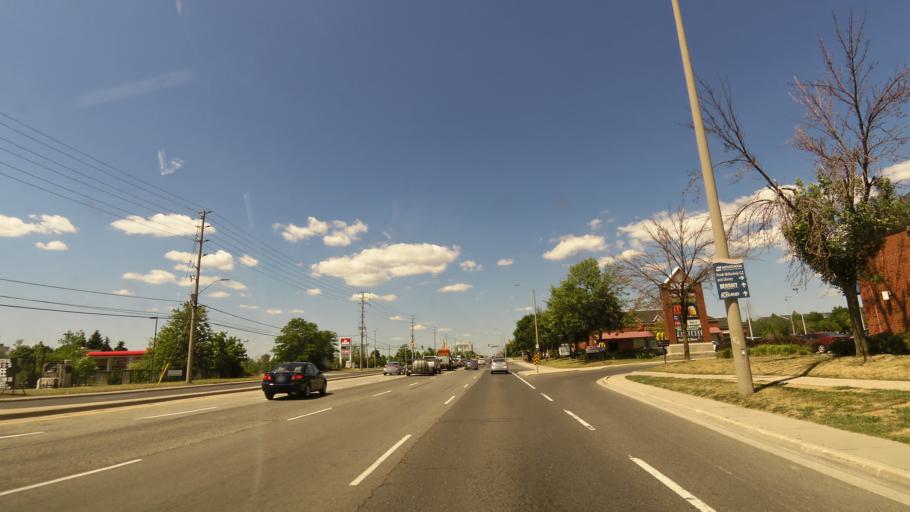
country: CA
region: Ontario
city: Mississauga
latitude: 43.6136
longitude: -79.6622
